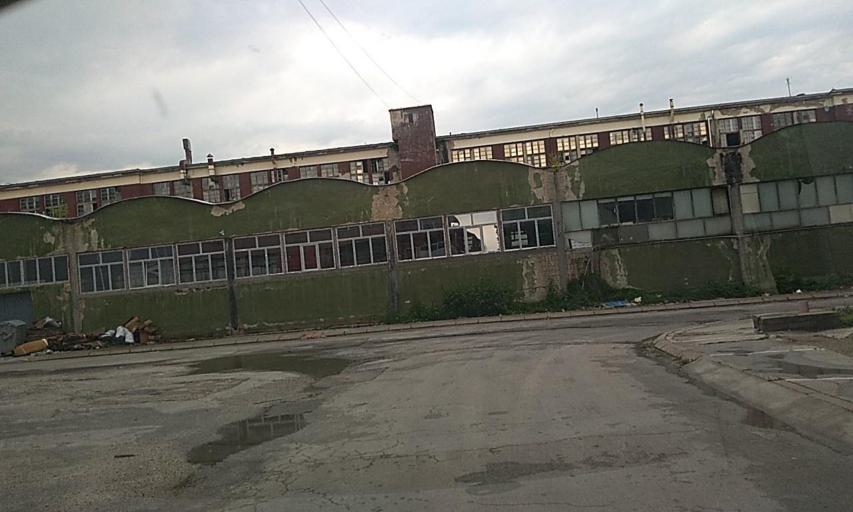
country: RS
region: Central Serbia
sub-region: Nisavski Okrug
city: Nis
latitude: 43.3050
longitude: 21.9506
